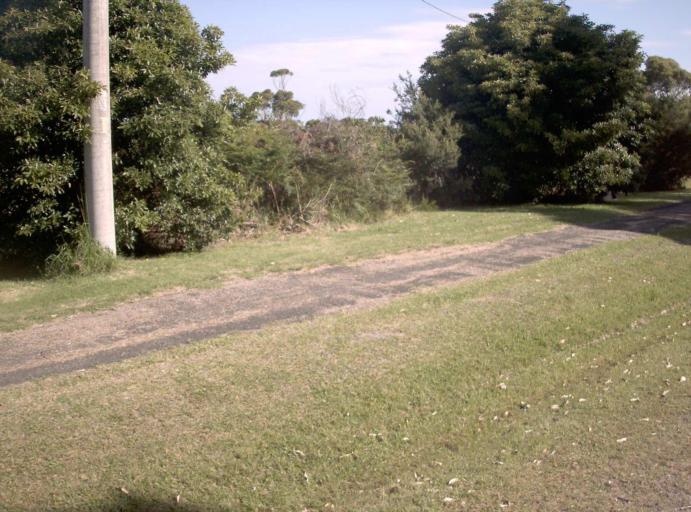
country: AU
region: Victoria
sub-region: East Gippsland
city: Lakes Entrance
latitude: -37.7921
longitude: 148.5347
